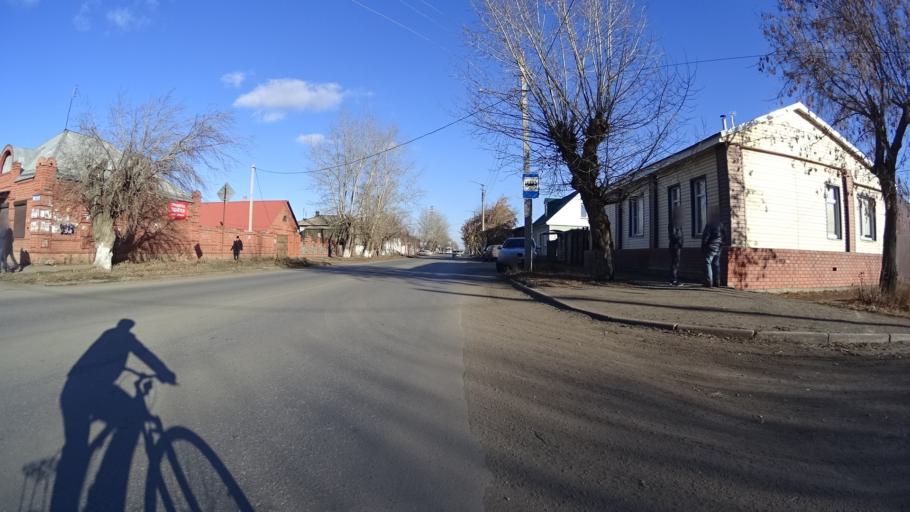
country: RU
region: Chelyabinsk
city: Troitsk
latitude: 54.0801
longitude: 61.5496
